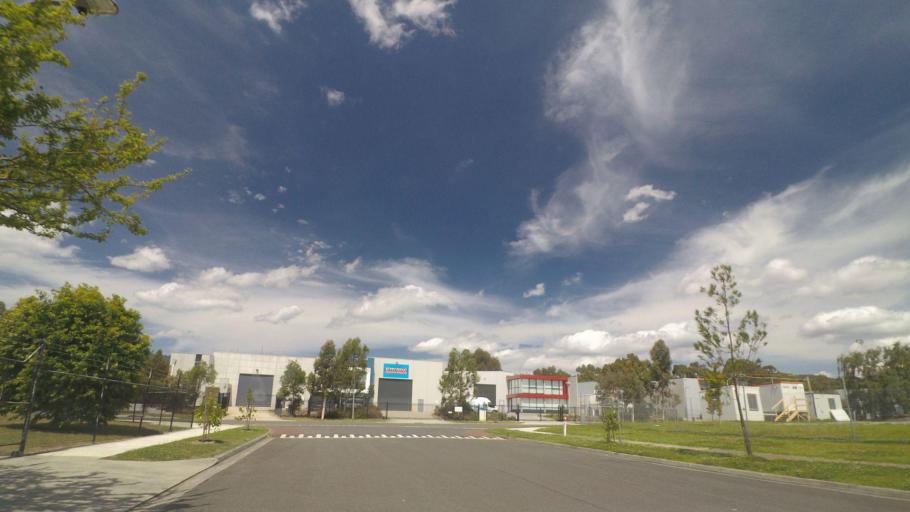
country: AU
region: Victoria
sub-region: Maroondah
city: Bayswater North
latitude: -37.8374
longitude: 145.2958
